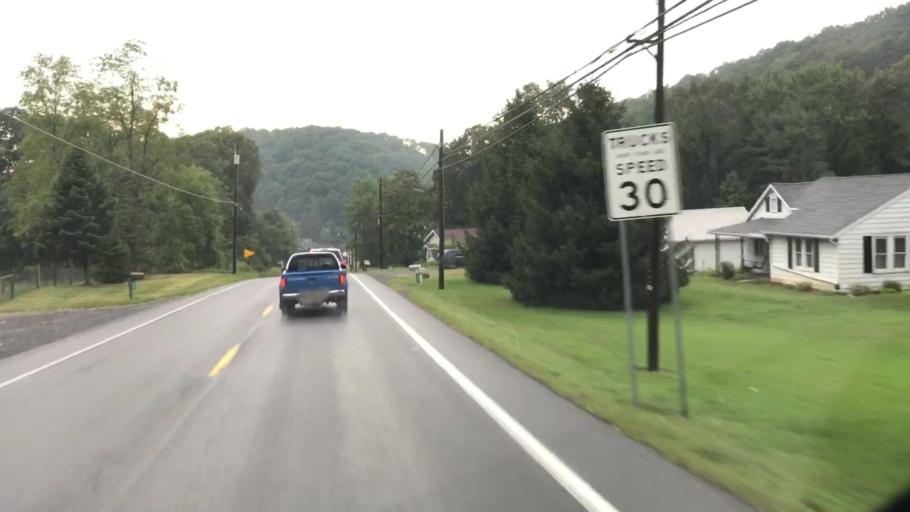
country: US
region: Pennsylvania
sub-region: Cumberland County
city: Schlusser
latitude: 40.3011
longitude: -77.1469
